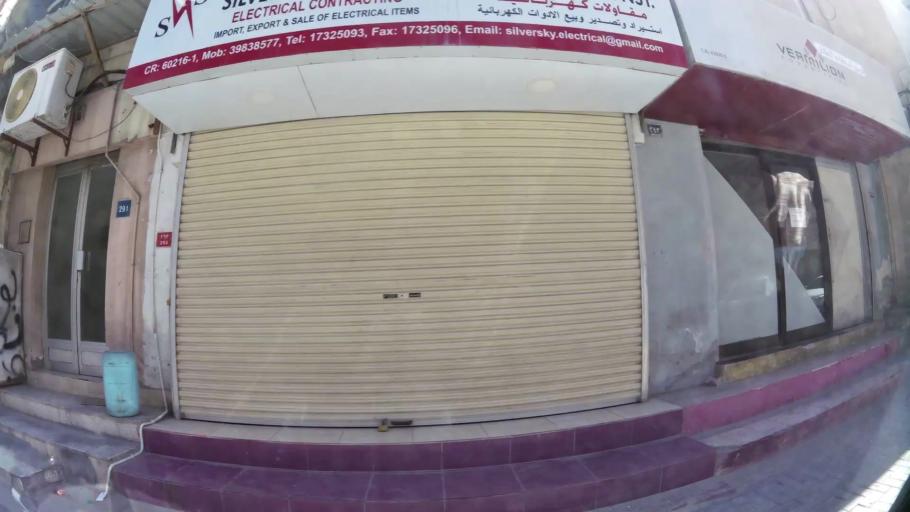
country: BH
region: Muharraq
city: Al Muharraq
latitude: 26.2473
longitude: 50.6124
